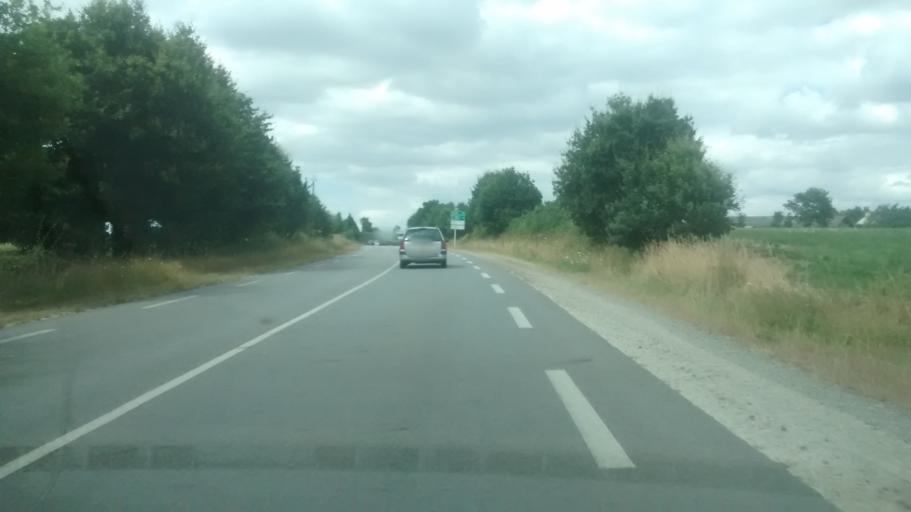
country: FR
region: Brittany
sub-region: Departement du Morbihan
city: Loyat
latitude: 47.9874
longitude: -2.3664
